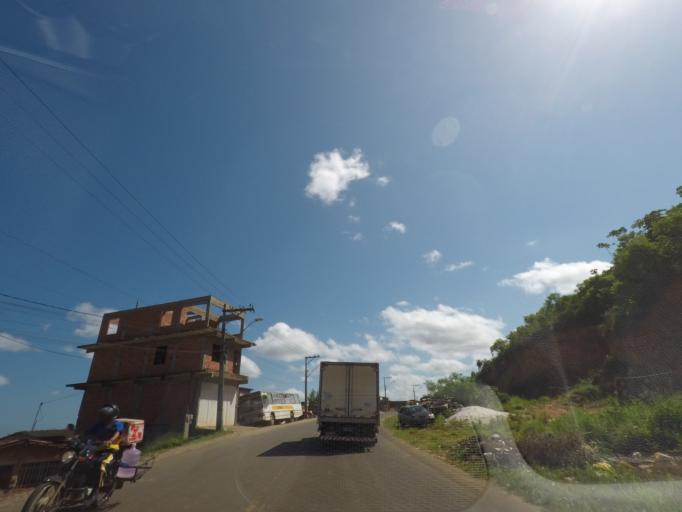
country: BR
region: Bahia
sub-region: Itubera
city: Itubera
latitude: -13.7442
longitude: -39.1512
